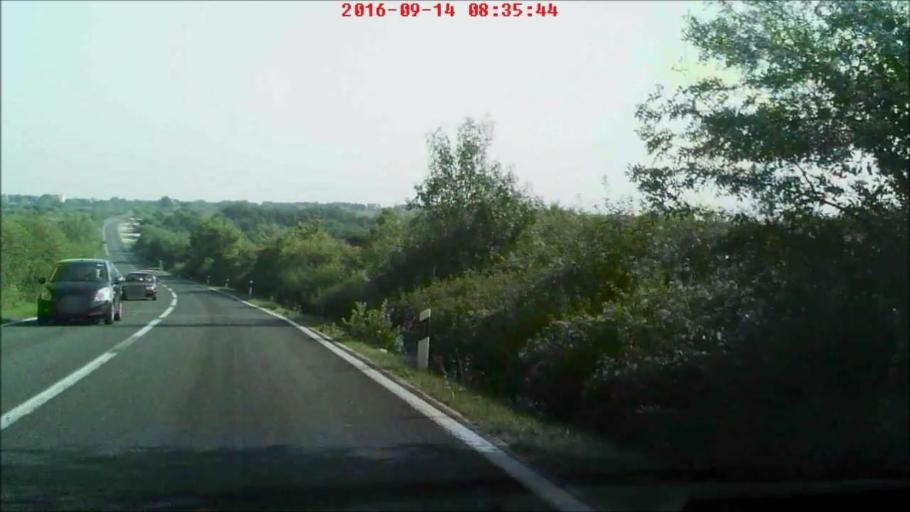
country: HR
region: Zadarska
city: Policnik
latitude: 44.1511
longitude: 15.3328
